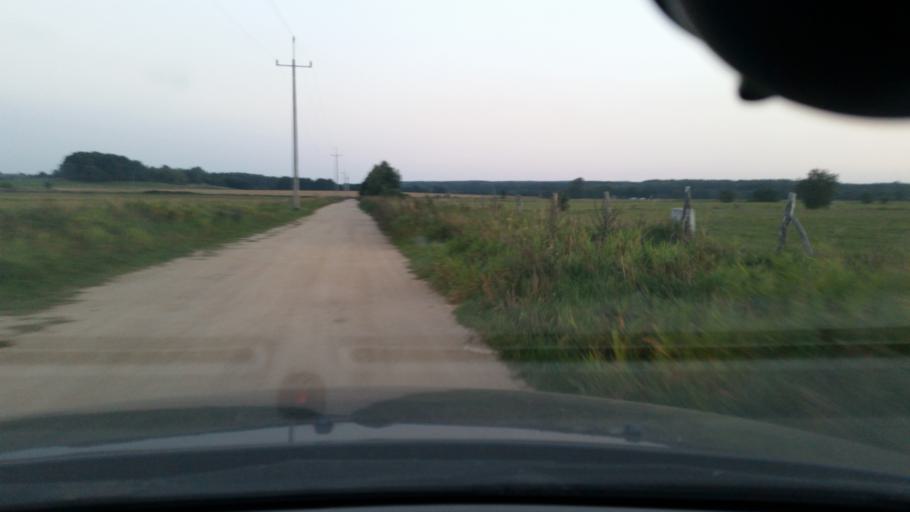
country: PL
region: Pomeranian Voivodeship
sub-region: Powiat wejherowski
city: Choczewo
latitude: 54.7791
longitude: 17.7925
